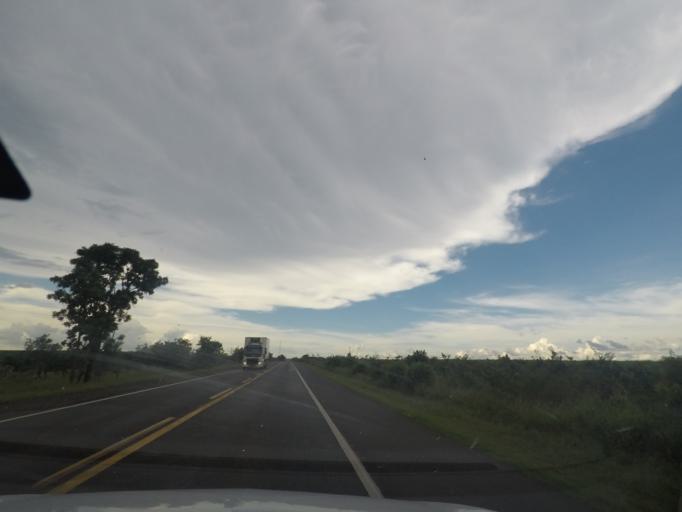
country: BR
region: Minas Gerais
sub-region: Prata
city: Prata
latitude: -19.6083
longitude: -48.8378
